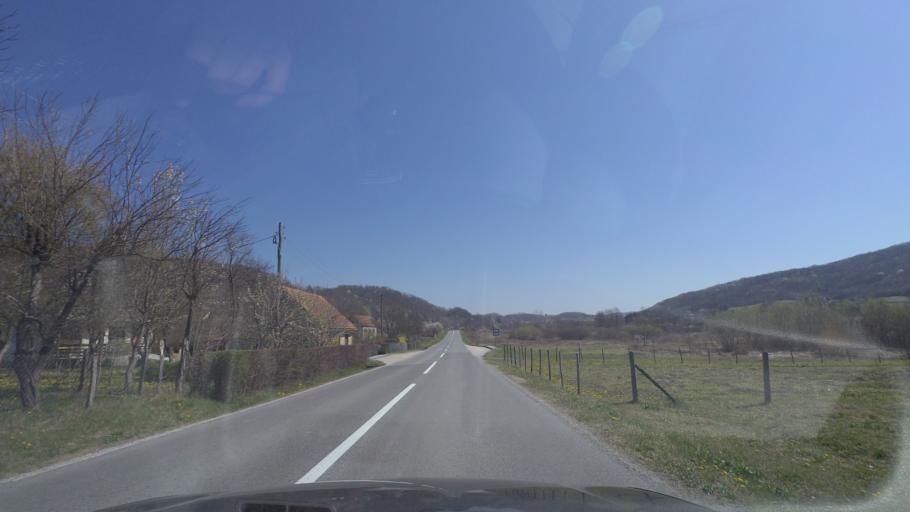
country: HR
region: Karlovacka
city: Vojnic
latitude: 45.3786
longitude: 15.6369
